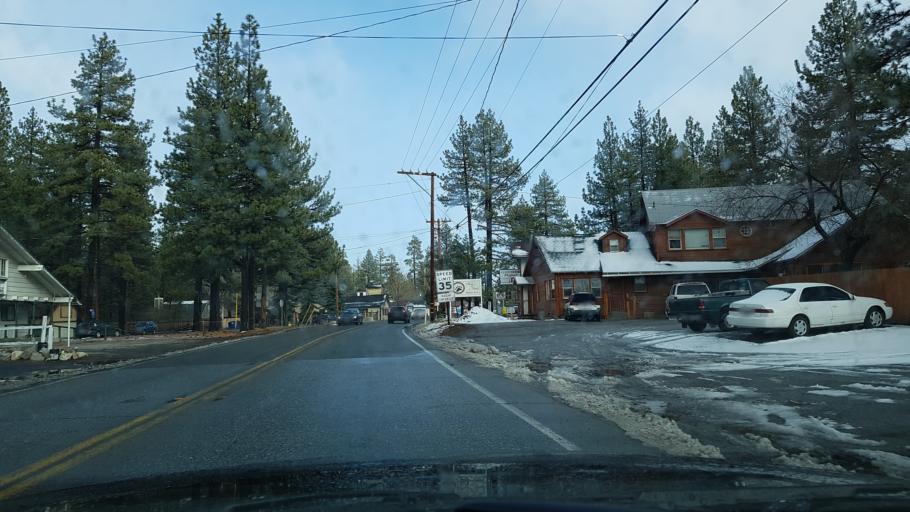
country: US
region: California
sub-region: San Bernardino County
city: Big Bear City
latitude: 34.2609
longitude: -116.8518
